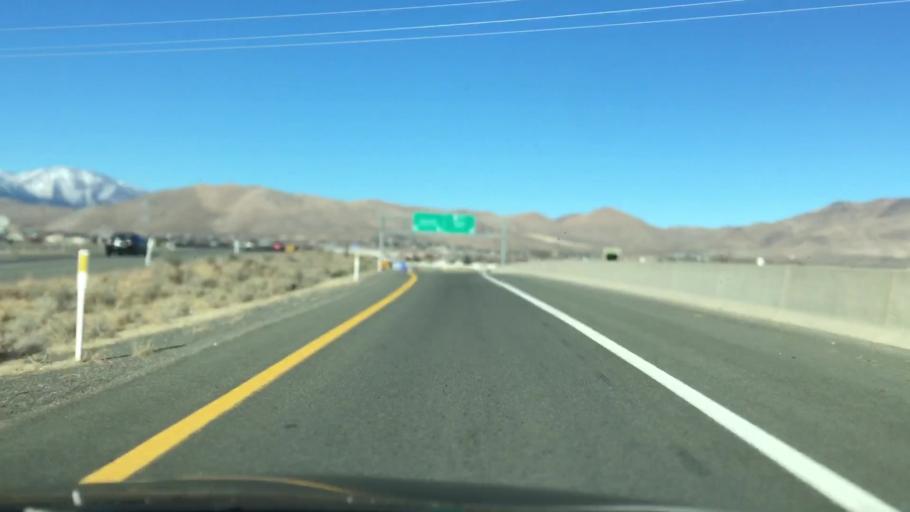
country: US
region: Nevada
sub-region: Carson City
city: Carson City
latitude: 39.1716
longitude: -119.7387
